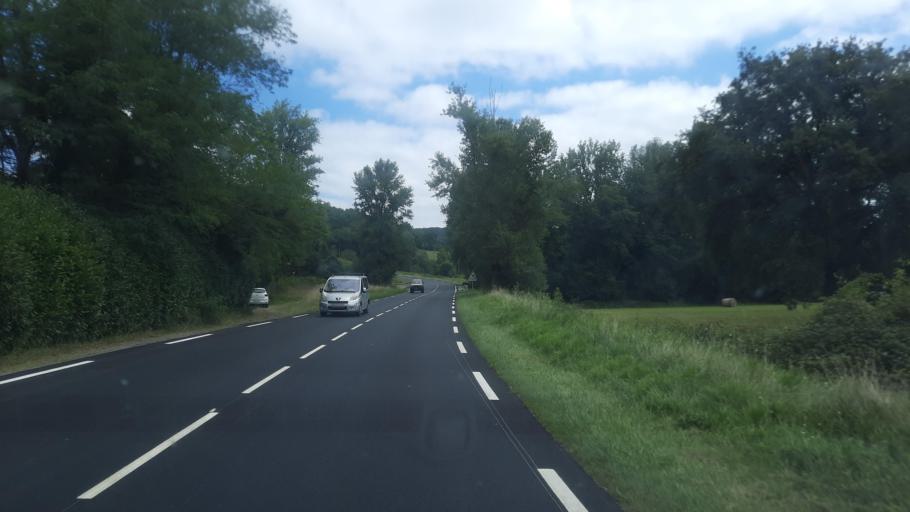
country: FR
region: Midi-Pyrenees
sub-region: Departement de la Haute-Garonne
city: Boulogne-sur-Gesse
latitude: 43.2864
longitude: 0.5432
